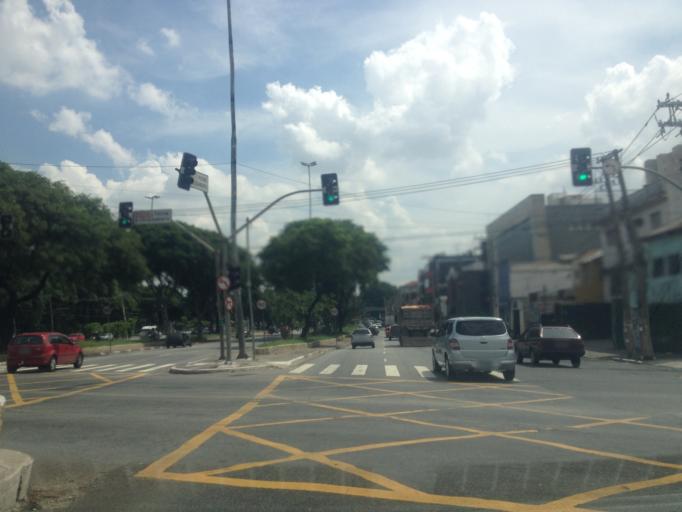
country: BR
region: Sao Paulo
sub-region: Sao Paulo
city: Sao Paulo
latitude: -23.5245
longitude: -46.6307
